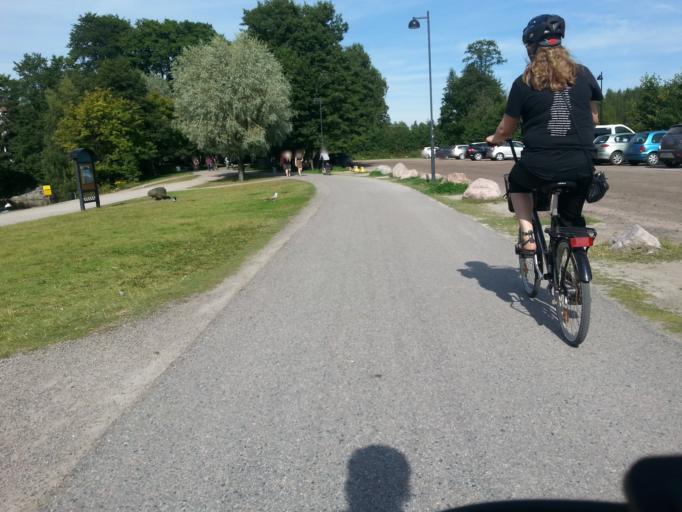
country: FI
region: Uusimaa
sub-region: Helsinki
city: Helsinki
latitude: 60.2144
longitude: 24.9851
